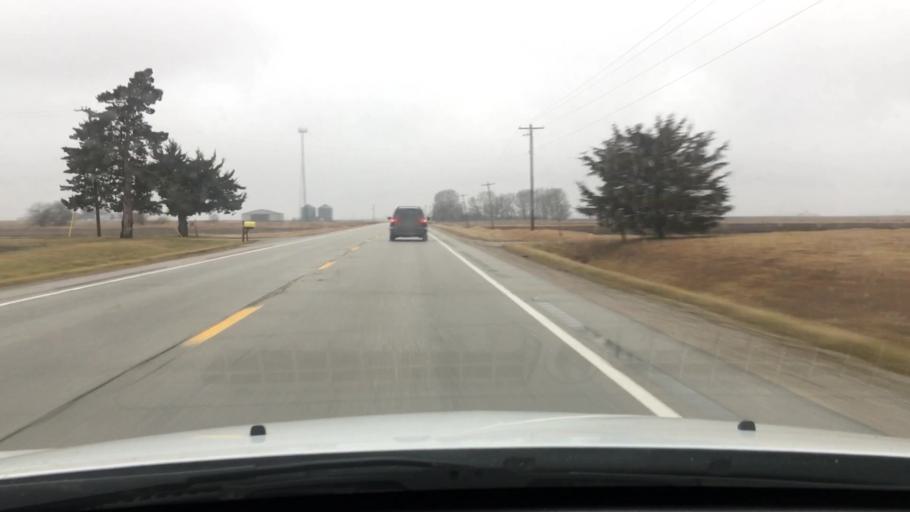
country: US
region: Illinois
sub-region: Livingston County
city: Flanagan
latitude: 40.8719
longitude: -88.8043
